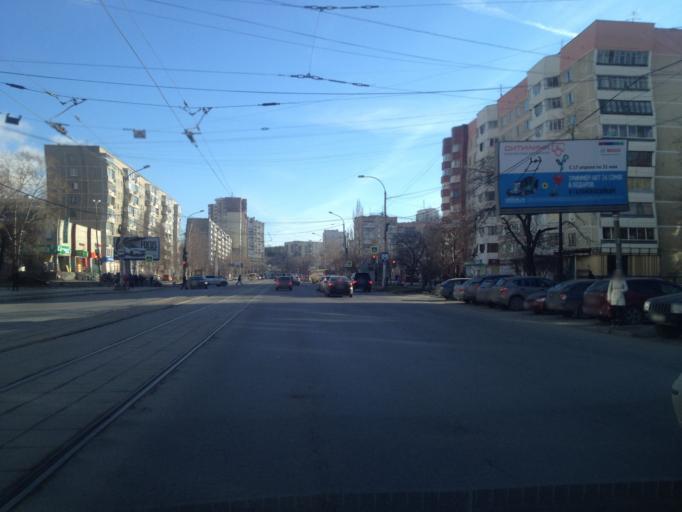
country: RU
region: Sverdlovsk
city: Yekaterinburg
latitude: 56.8206
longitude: 60.5681
